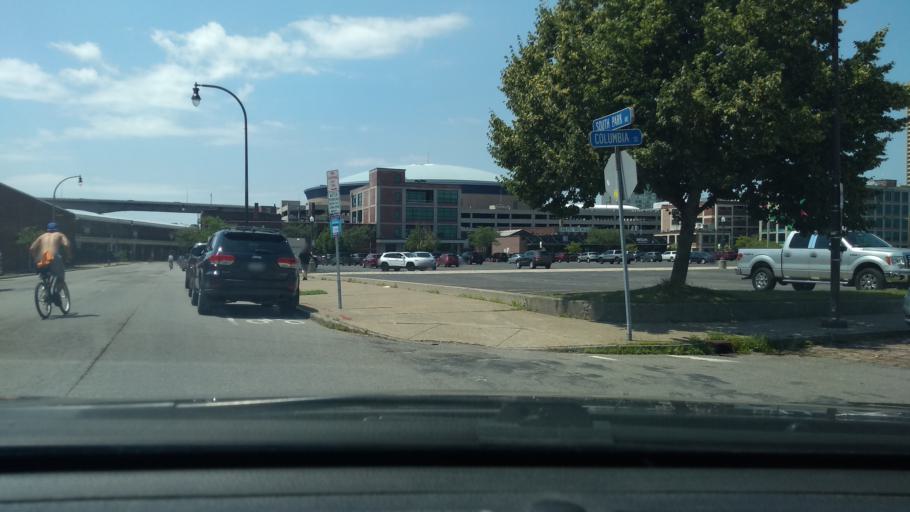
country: US
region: New York
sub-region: Erie County
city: Buffalo
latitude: 42.8732
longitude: -78.8728
